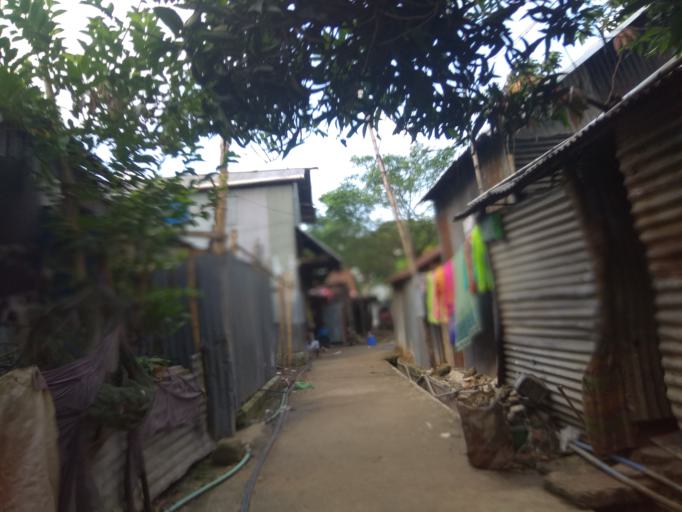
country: BD
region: Dhaka
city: Paltan
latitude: 23.8098
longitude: 90.3883
